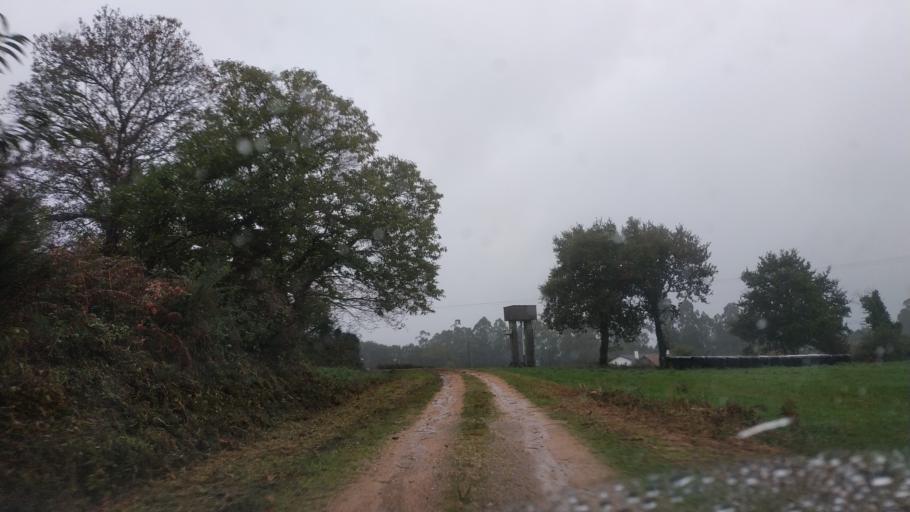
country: ES
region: Galicia
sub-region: Provincia da Coruna
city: Negreira
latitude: 42.9093
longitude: -8.7628
